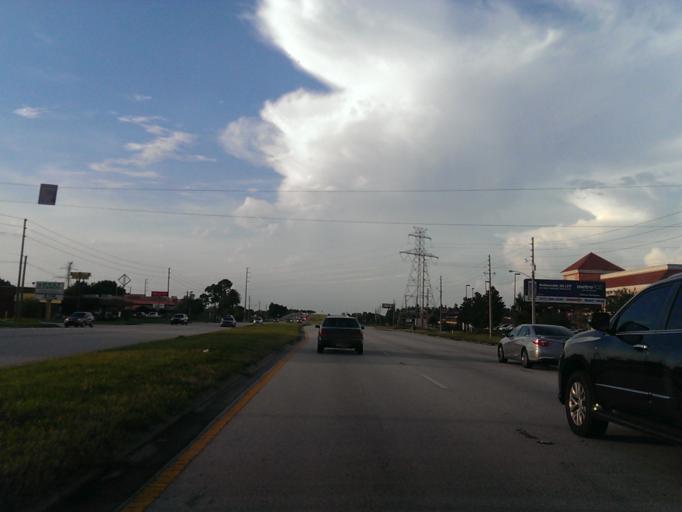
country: US
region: Florida
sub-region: Orange County
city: Tangelo Park
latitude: 28.4833
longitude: -81.4588
